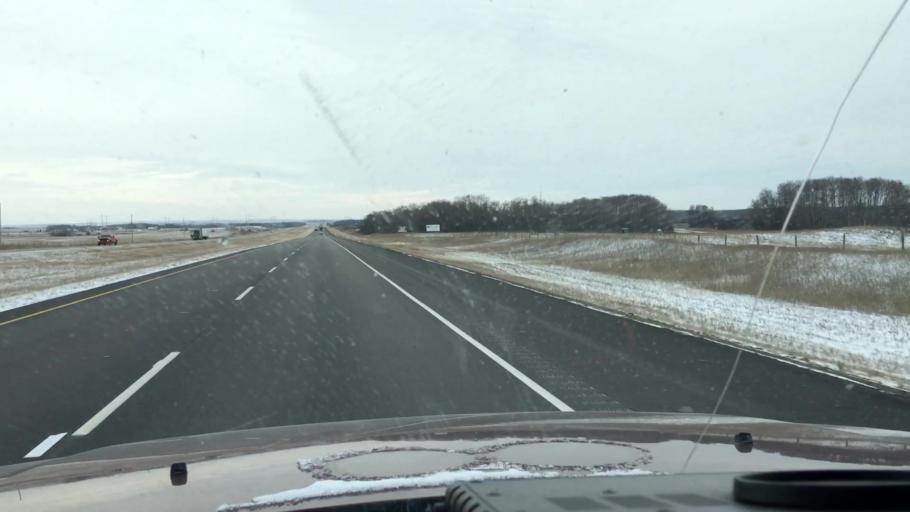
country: CA
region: Saskatchewan
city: Saskatoon
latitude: 51.9037
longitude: -106.5231
